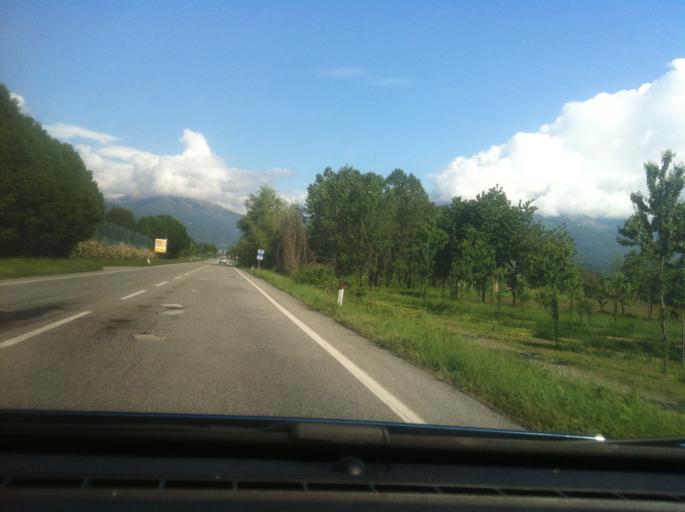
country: IT
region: Piedmont
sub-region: Provincia di Torino
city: Salassa
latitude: 45.3590
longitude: 7.6929
